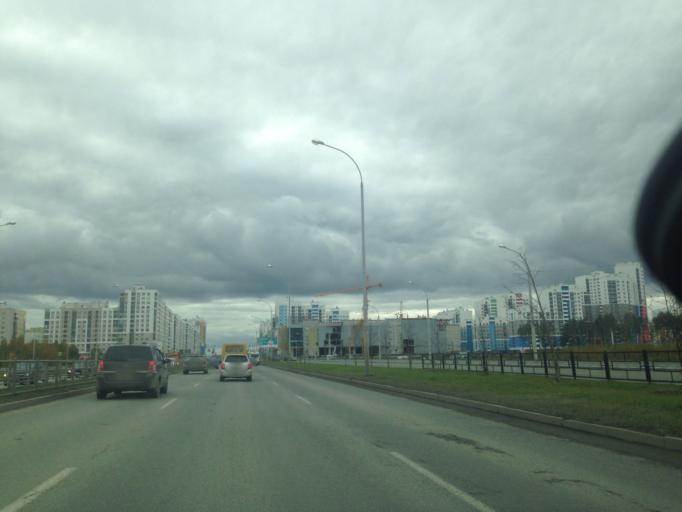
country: RU
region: Sverdlovsk
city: Sovkhoznyy
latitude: 56.7957
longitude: 60.5261
